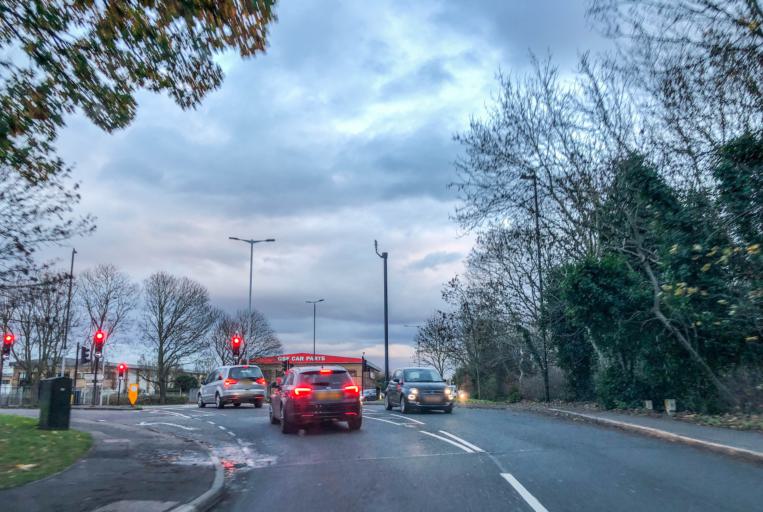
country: GB
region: England
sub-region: Greater London
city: Feltham
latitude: 51.4635
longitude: -0.4157
